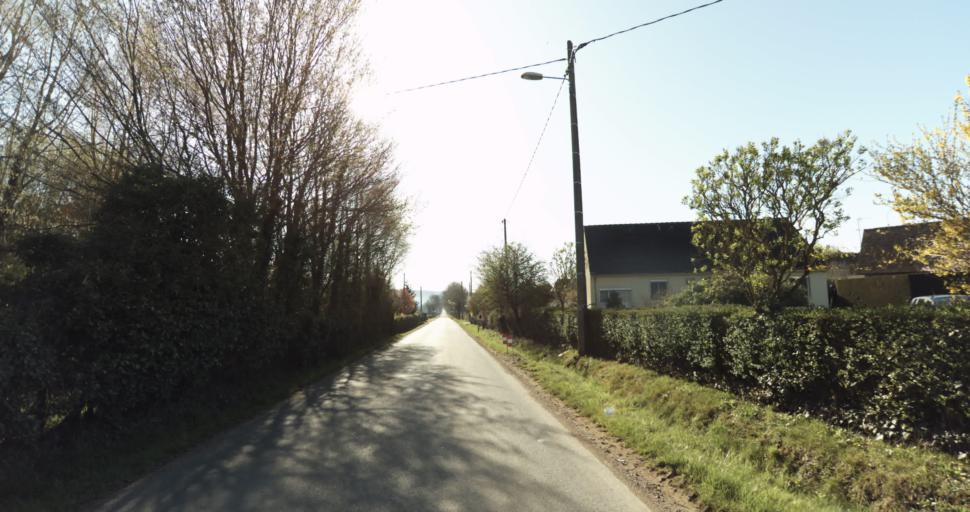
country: FR
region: Lower Normandy
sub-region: Departement du Calvados
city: Saint-Pierre-sur-Dives
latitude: 49.0040
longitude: -0.0067
